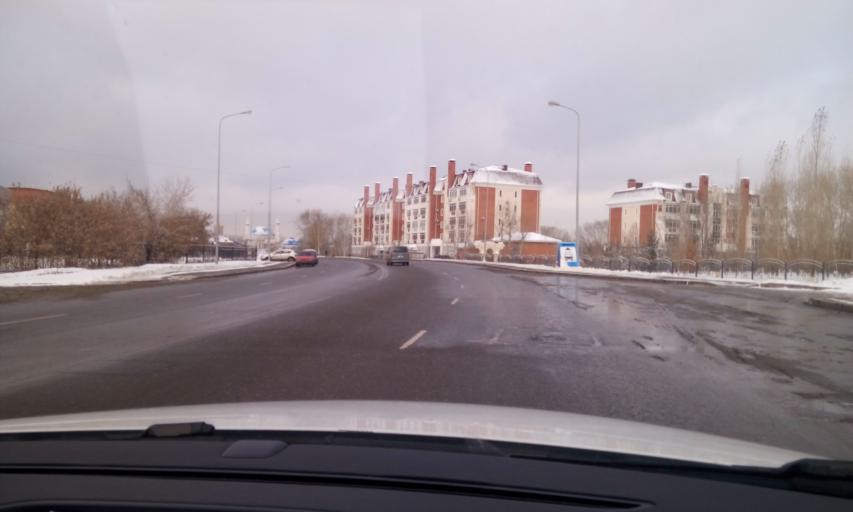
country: KZ
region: Astana Qalasy
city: Astana
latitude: 51.1355
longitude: 71.4355
